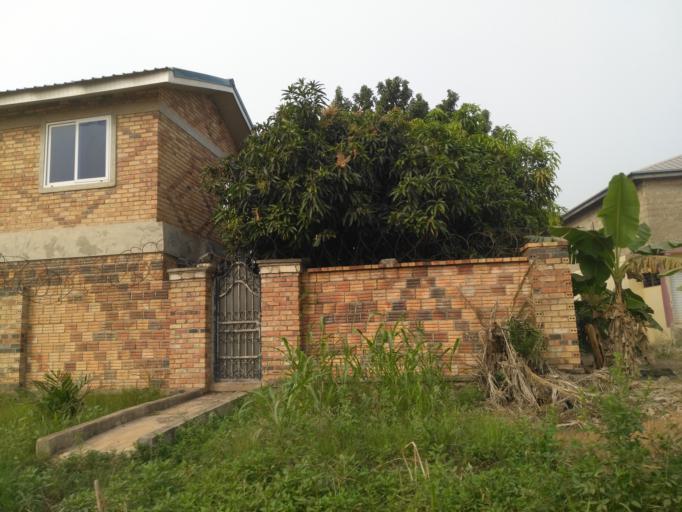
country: GH
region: Ashanti
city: Kumasi
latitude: 6.6573
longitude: -1.6264
